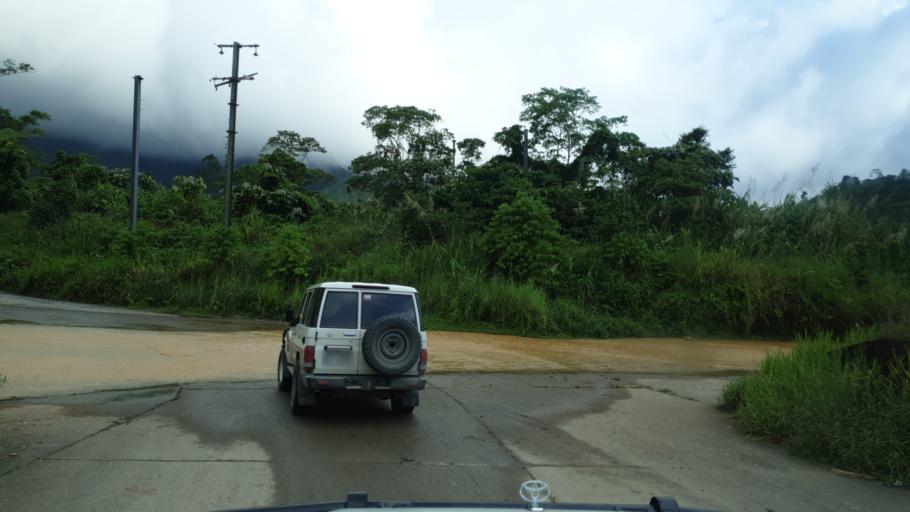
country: PG
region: Bougainville
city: Panguna
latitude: -6.3071
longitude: 155.4877
